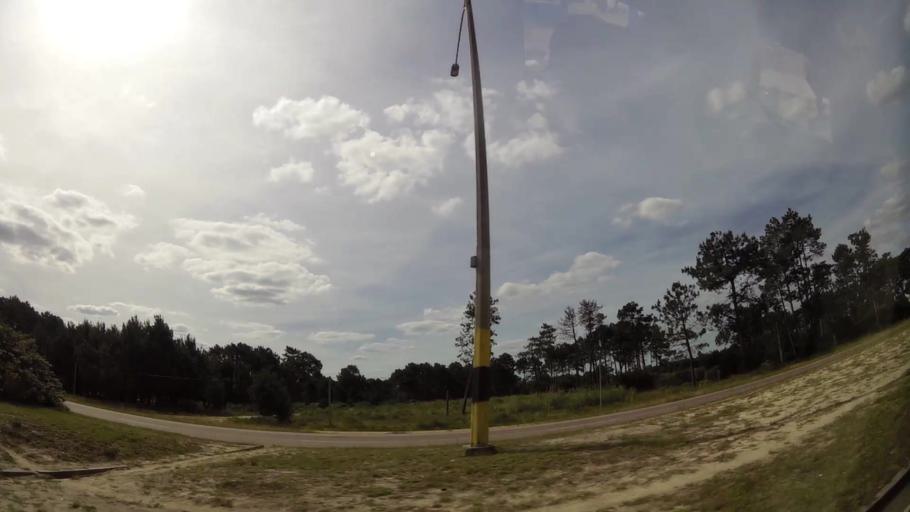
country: UY
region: Canelones
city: Pando
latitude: -34.7975
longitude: -55.9135
